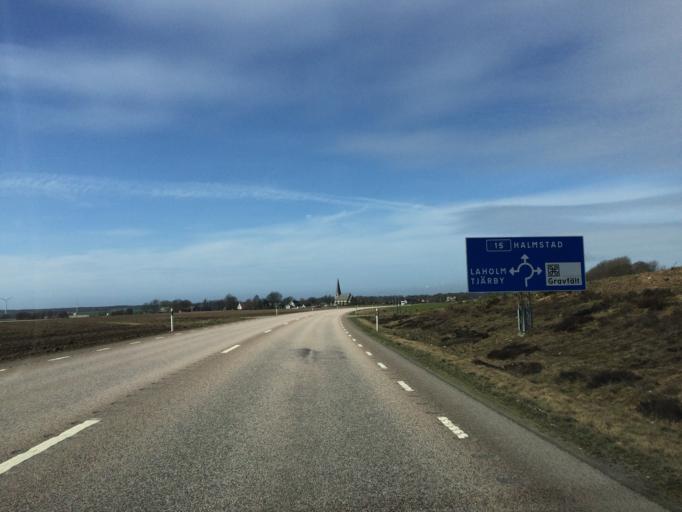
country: SE
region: Halland
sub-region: Laholms Kommun
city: Veinge
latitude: 56.5442
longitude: 13.0579
